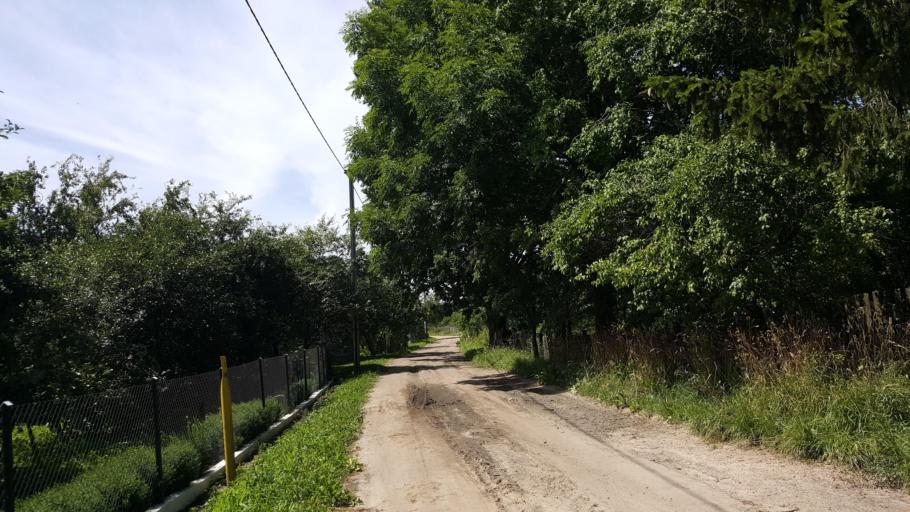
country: BY
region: Brest
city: Pruzhany
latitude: 52.5617
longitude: 24.2223
